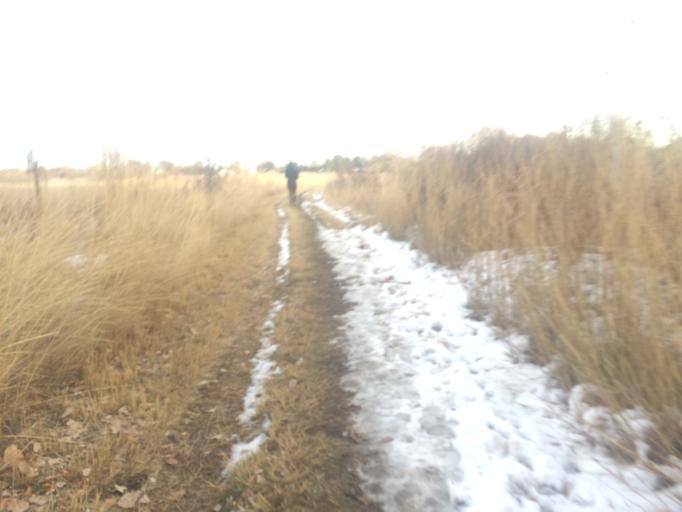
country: US
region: Colorado
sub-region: Boulder County
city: Gunbarrel
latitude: 40.0232
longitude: -105.1545
